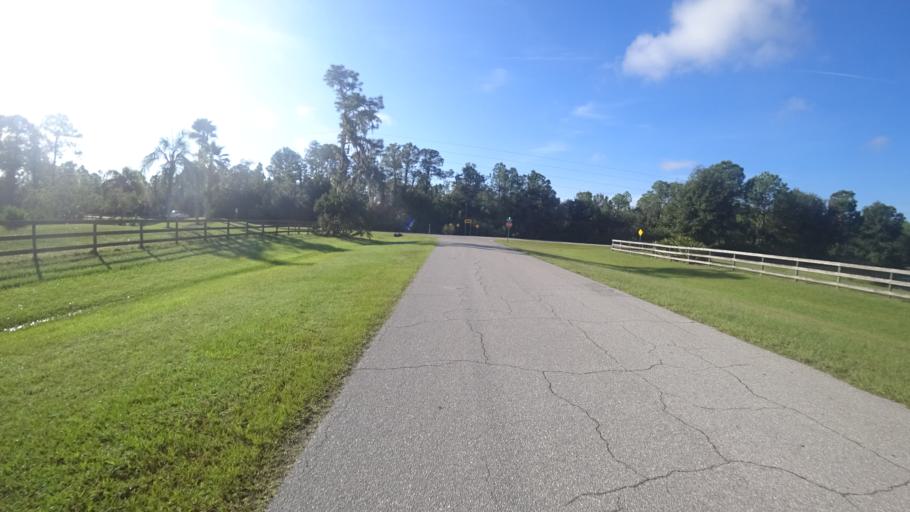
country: US
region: Florida
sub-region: Sarasota County
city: The Meadows
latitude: 27.4177
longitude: -82.3438
